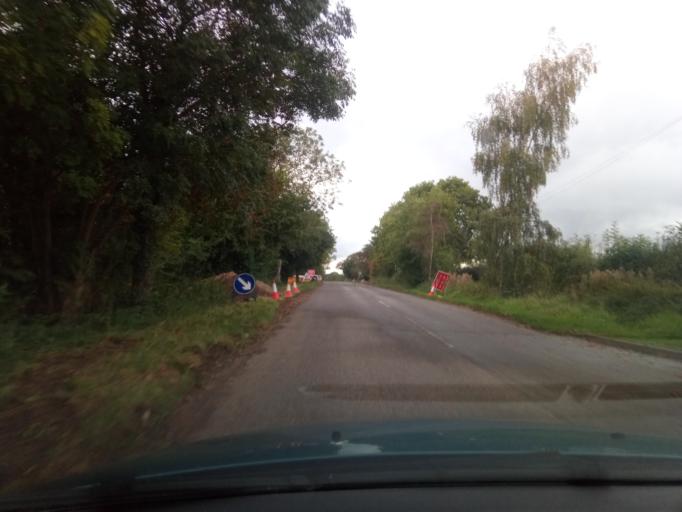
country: GB
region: England
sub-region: Leicestershire
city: Sileby
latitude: 52.7458
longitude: -1.0722
